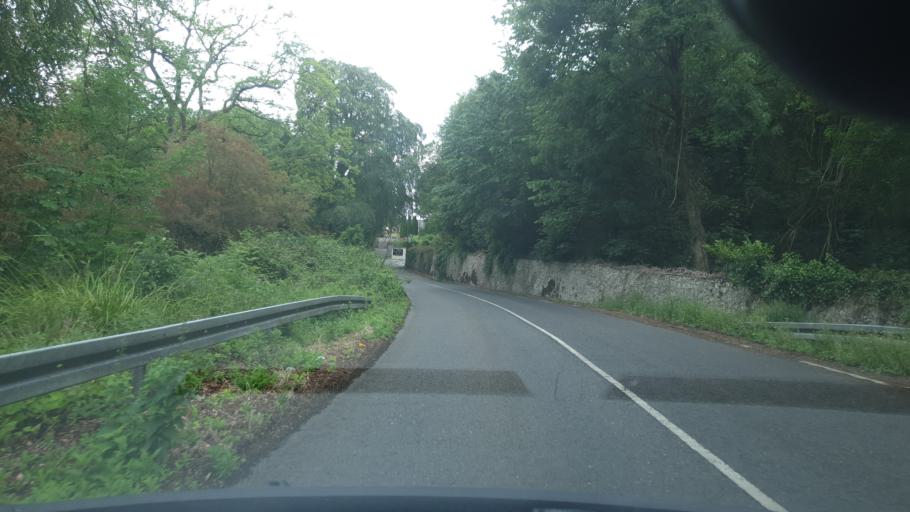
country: IE
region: Munster
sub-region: Ciarrai
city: Tralee
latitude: 52.2555
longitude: -9.6426
